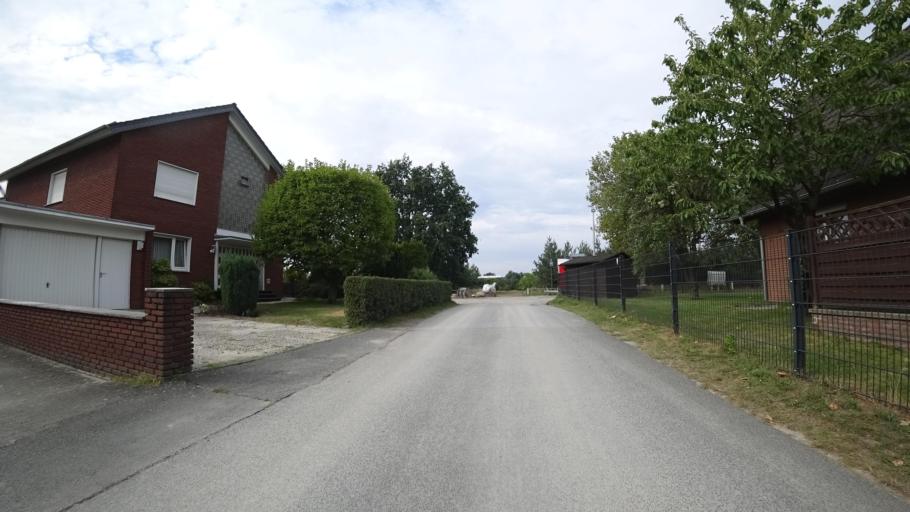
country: DE
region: North Rhine-Westphalia
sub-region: Regierungsbezirk Detmold
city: Guetersloh
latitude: 51.9158
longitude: 8.4111
